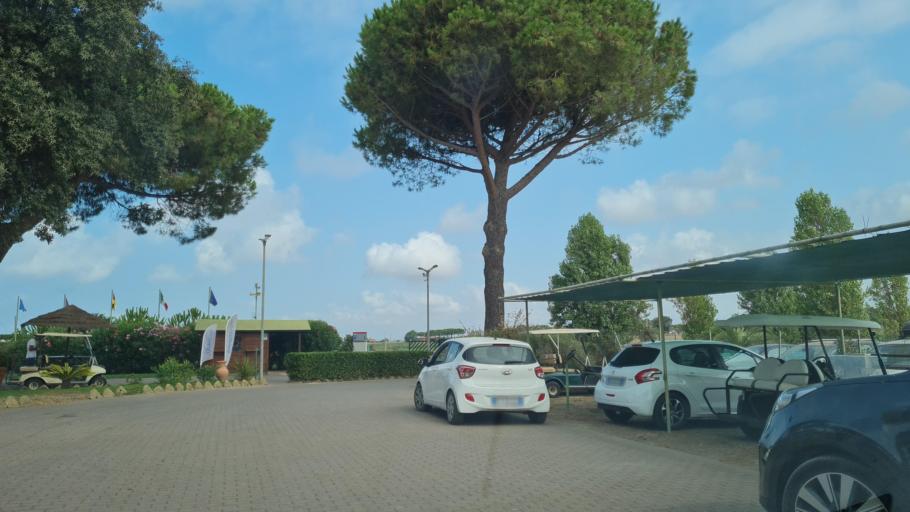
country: IT
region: Latium
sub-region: Provincia di Viterbo
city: Montalto di Castro
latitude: 42.3050
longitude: 11.6232
